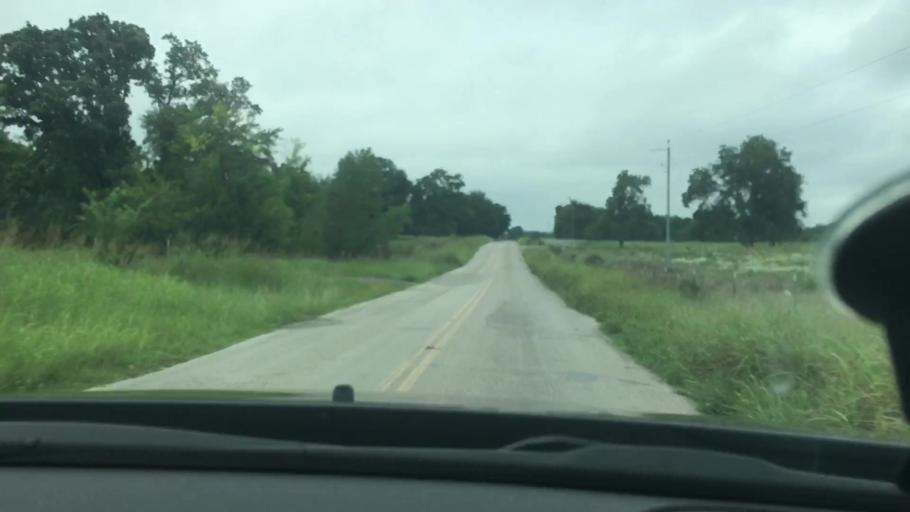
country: US
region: Oklahoma
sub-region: Pontotoc County
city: Ada
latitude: 34.8102
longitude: -96.7573
